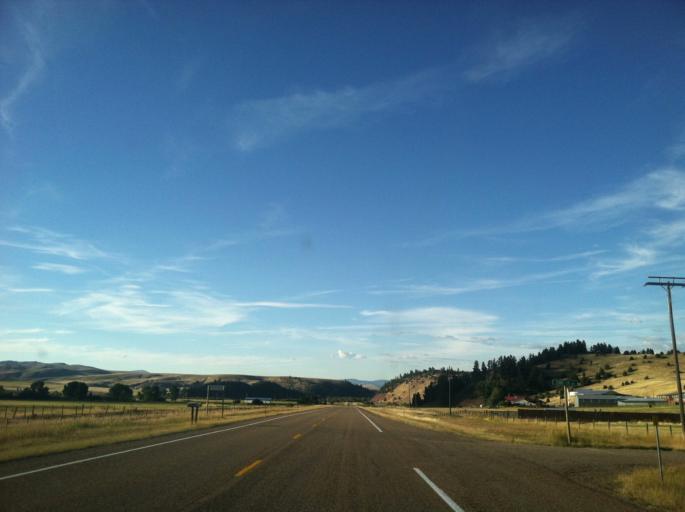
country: US
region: Montana
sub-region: Granite County
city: Philipsburg
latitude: 46.4961
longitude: -113.2224
